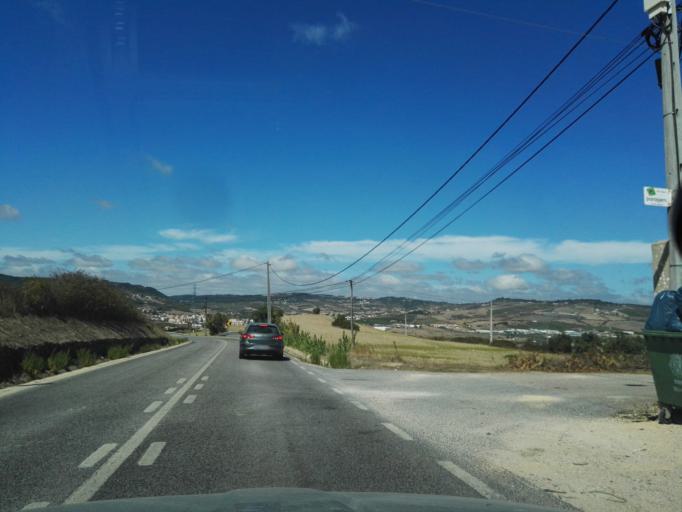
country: PT
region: Lisbon
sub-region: Arruda Dos Vinhos
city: Arruda dos Vinhos
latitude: 38.9746
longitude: -9.0509
